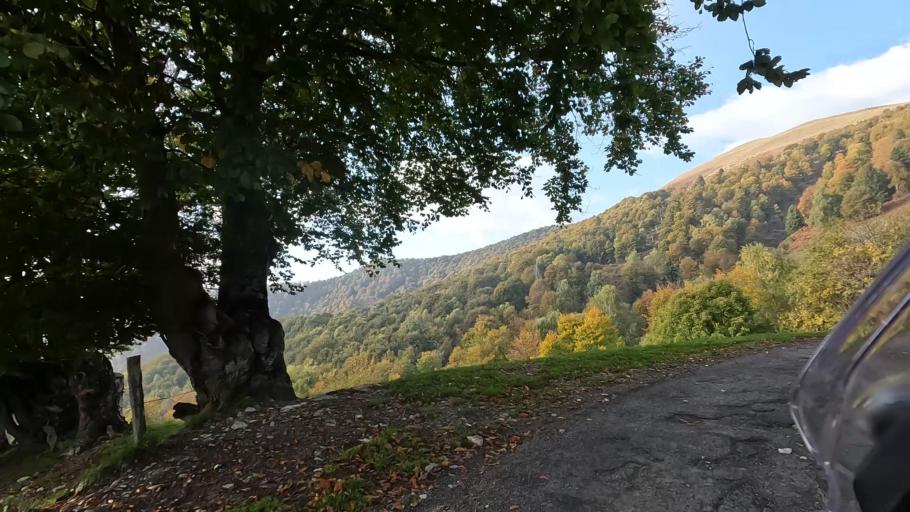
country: IT
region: Lombardy
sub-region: Provincia di Como
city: Sala Comacina
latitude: 45.9928
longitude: 9.1473
